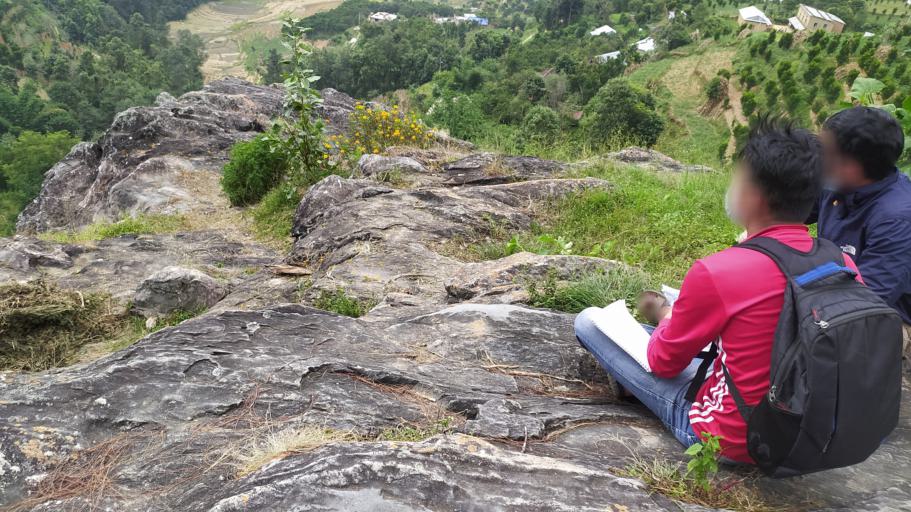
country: NP
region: Central Region
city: Panaoti
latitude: 27.5872
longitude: 85.5369
